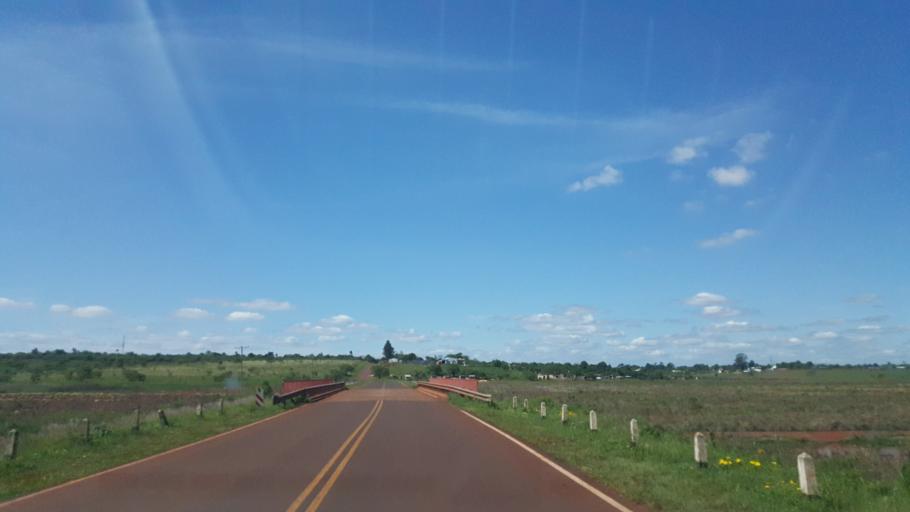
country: AR
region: Misiones
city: Garupa
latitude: -27.4933
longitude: -55.8379
